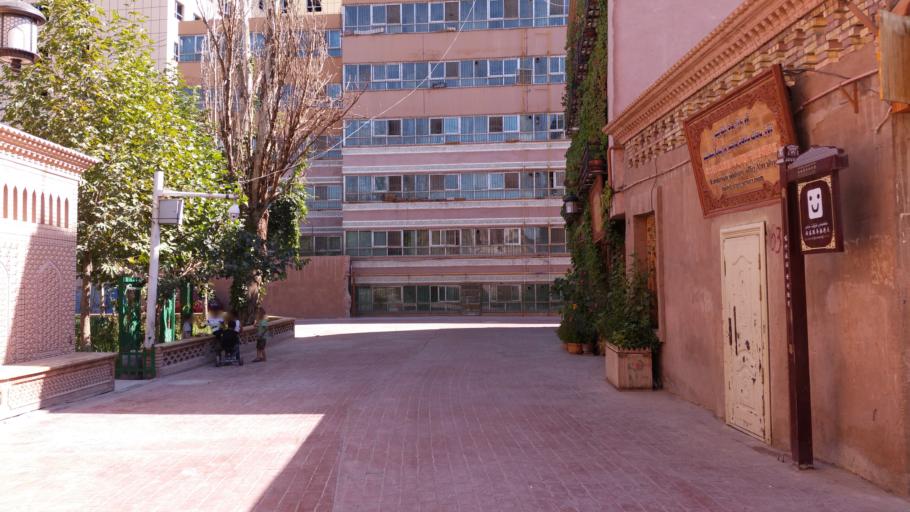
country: CN
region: Xinjiang Uygur Zizhiqu
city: Kashi
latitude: 39.4680
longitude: 75.9813
